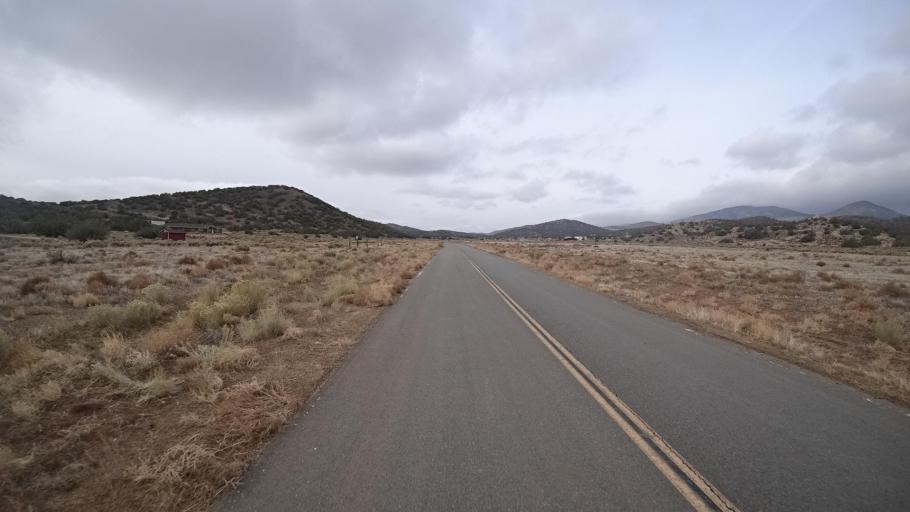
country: US
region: California
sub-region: Kern County
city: Tehachapi
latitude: 35.1730
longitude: -118.3380
